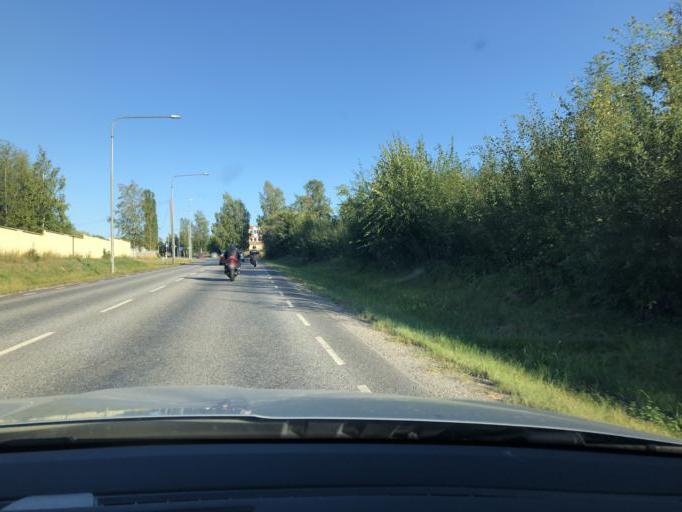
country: SE
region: Stockholm
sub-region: Sodertalje Kommun
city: Soedertaelje
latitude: 59.1841
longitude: 17.5928
